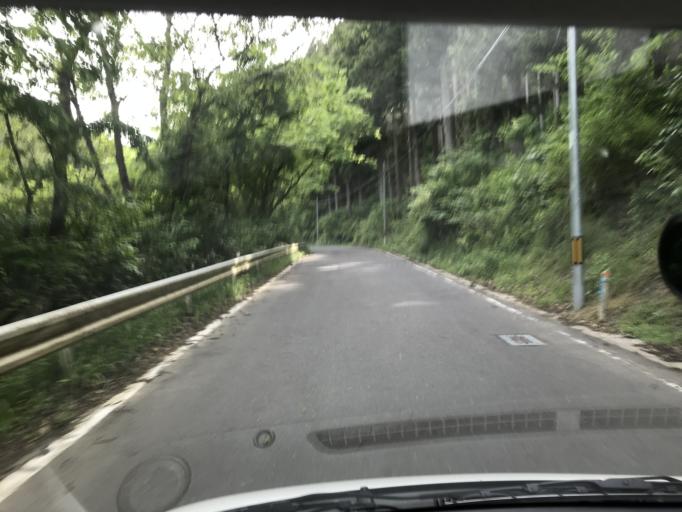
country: JP
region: Miyagi
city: Wakuya
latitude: 38.6699
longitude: 141.3403
